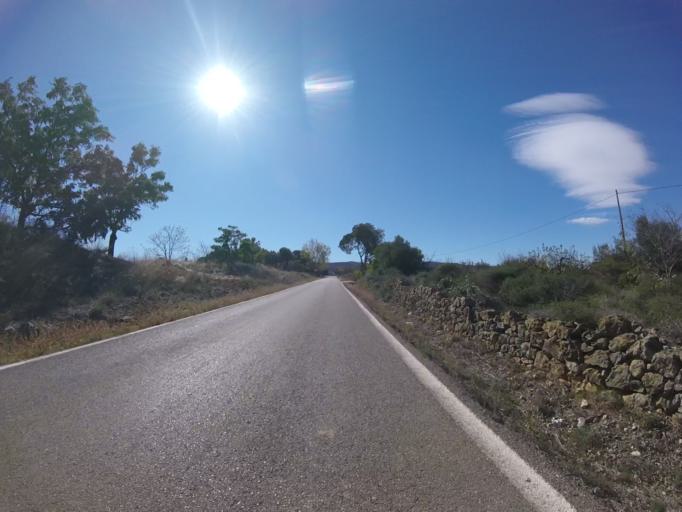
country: ES
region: Valencia
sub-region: Provincia de Castello
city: Albocasser
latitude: 40.3674
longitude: 0.0204
